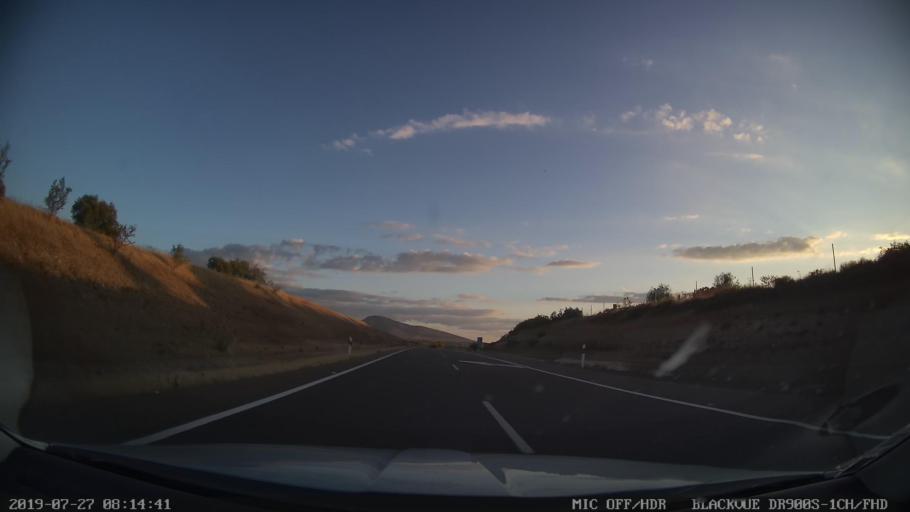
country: ES
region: Extremadura
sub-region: Provincia de Badajoz
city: Calamonte
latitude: 38.9095
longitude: -6.3812
